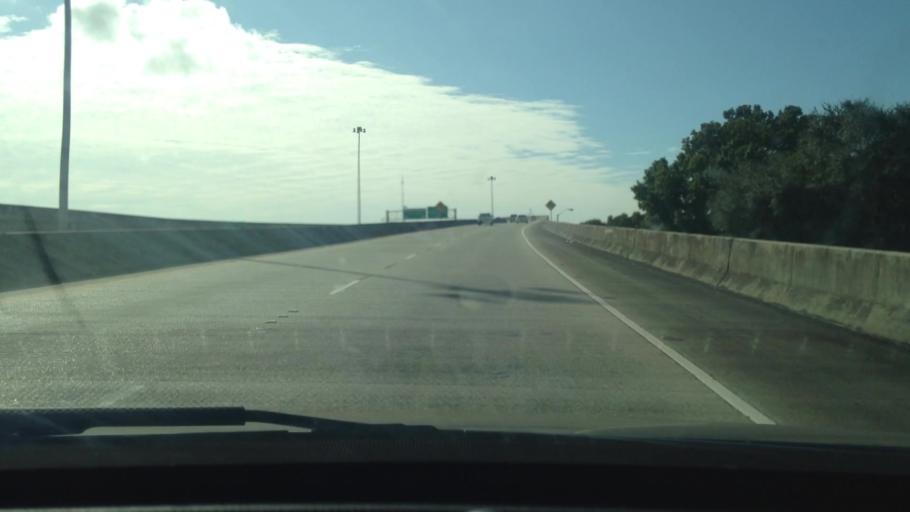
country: US
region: Louisiana
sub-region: Jefferson Parish
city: Terrytown
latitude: 29.9335
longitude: -90.0384
